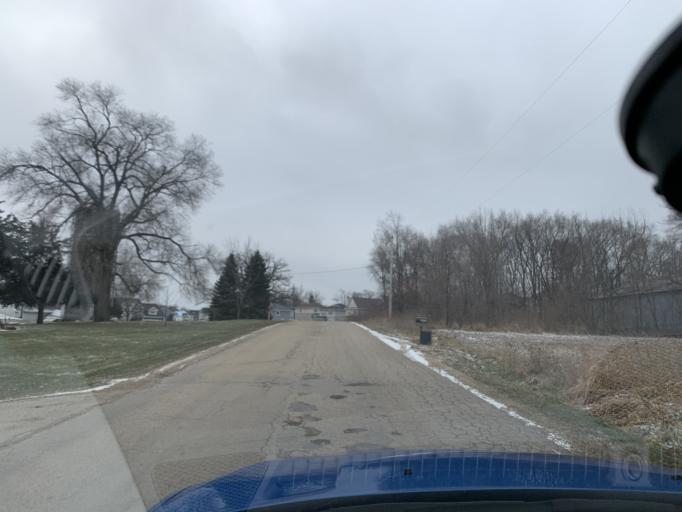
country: US
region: Wisconsin
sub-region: Dane County
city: Middleton
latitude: 43.0725
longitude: -89.5633
